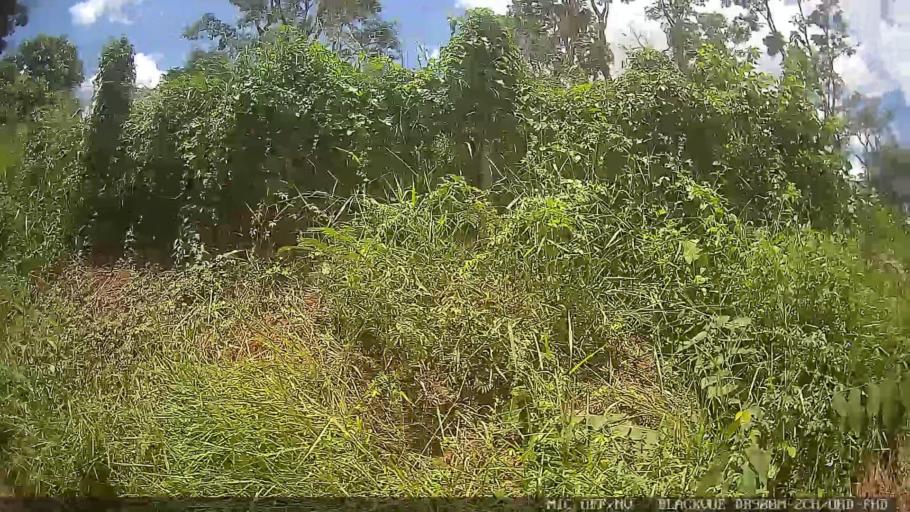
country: BR
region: Minas Gerais
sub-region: Extrema
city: Extrema
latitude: -22.8550
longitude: -46.2801
